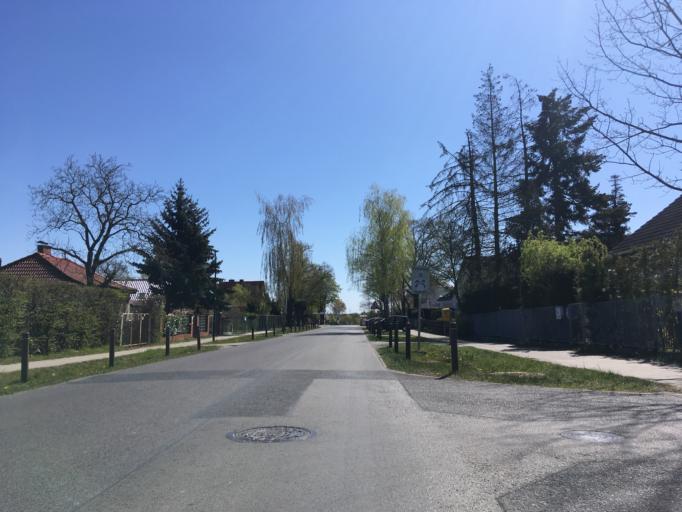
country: DE
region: Brandenburg
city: Bernau bei Berlin
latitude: 52.6437
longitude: 13.5580
